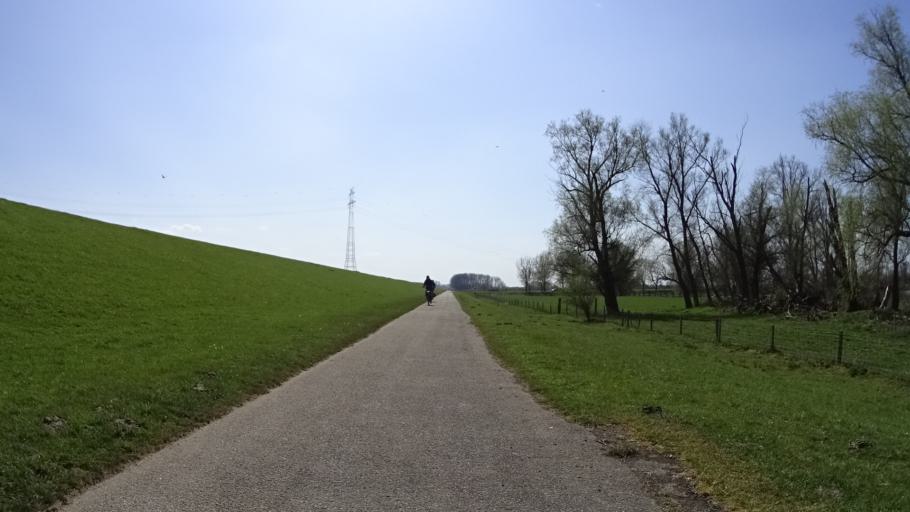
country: DE
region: Lower Saxony
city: Weener
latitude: 53.1531
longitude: 7.3712
